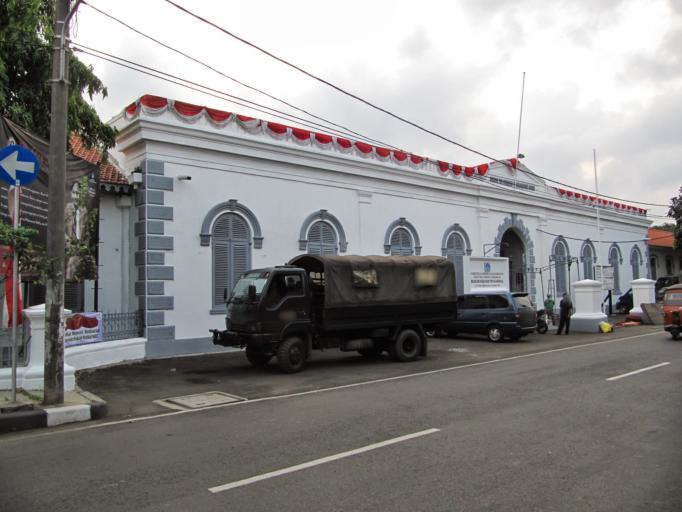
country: ID
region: Jakarta Raya
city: Jakarta
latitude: -6.1787
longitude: 106.8385
